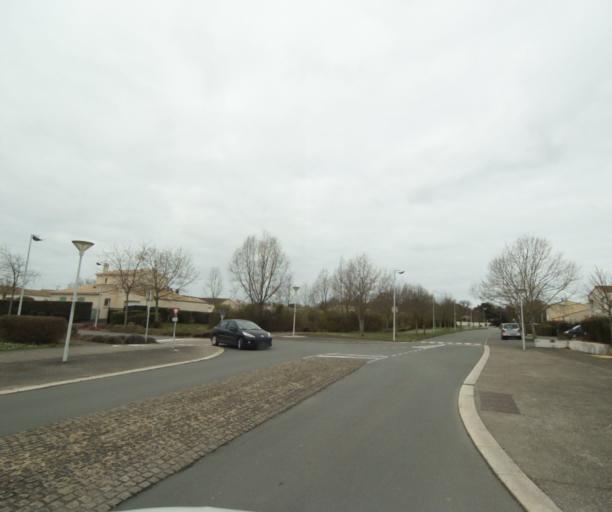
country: FR
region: Poitou-Charentes
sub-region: Departement de la Charente-Maritime
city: Lagord
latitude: 46.1879
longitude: -1.1599
